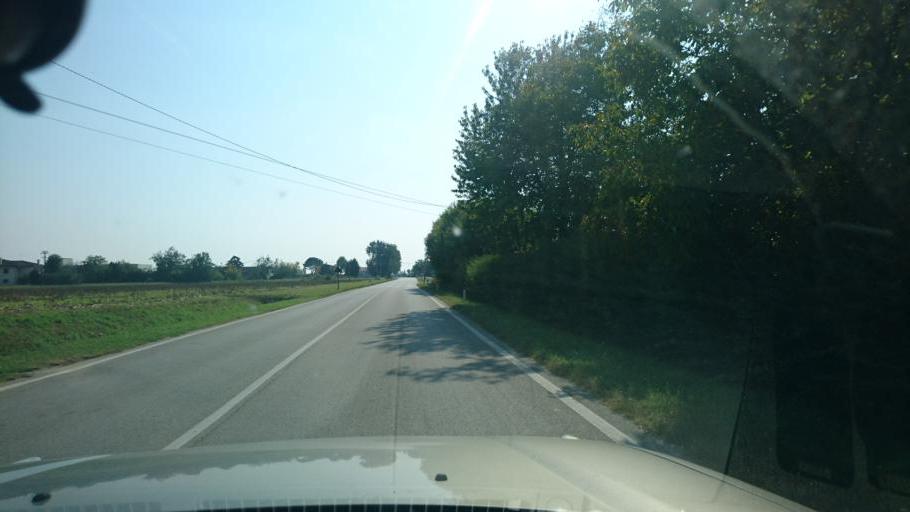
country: IT
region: Veneto
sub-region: Provincia di Padova
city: Campodoro
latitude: 45.5045
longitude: 11.7427
